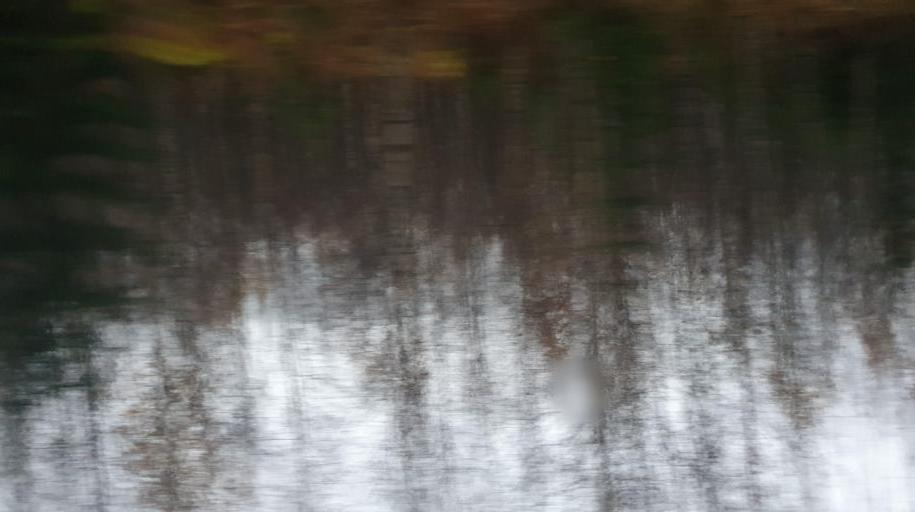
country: NO
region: Buskerud
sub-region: Krodsherad
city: Noresund
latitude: 60.1905
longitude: 9.5934
